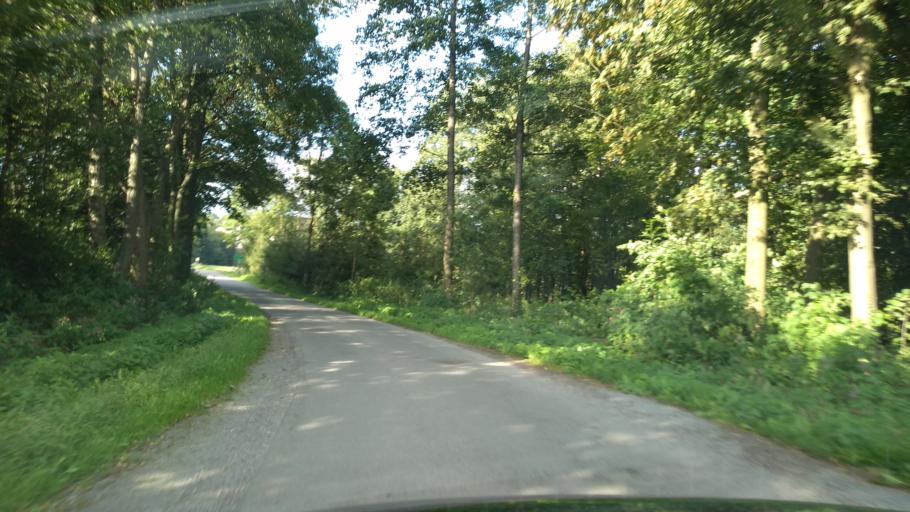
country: DE
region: North Rhine-Westphalia
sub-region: Regierungsbezirk Koln
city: Much
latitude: 50.8678
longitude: 7.3805
